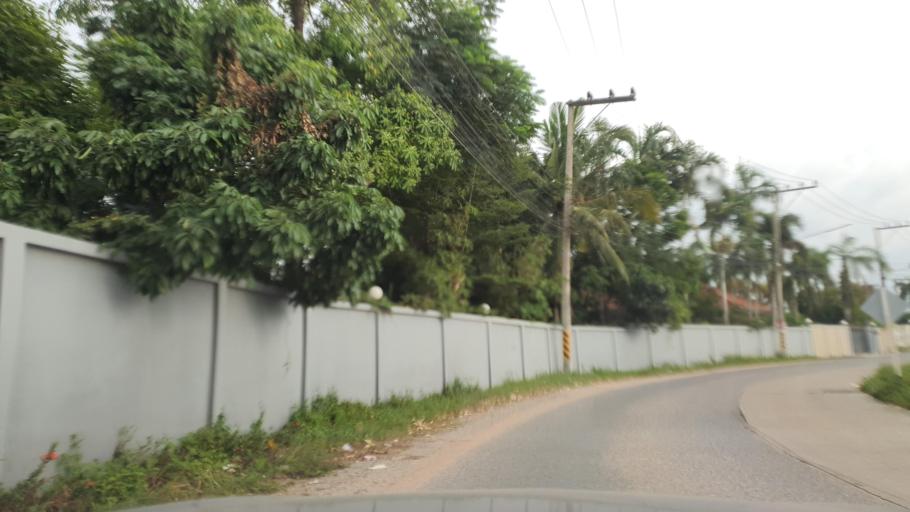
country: TH
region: Chon Buri
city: Phatthaya
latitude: 12.9497
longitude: 100.9395
